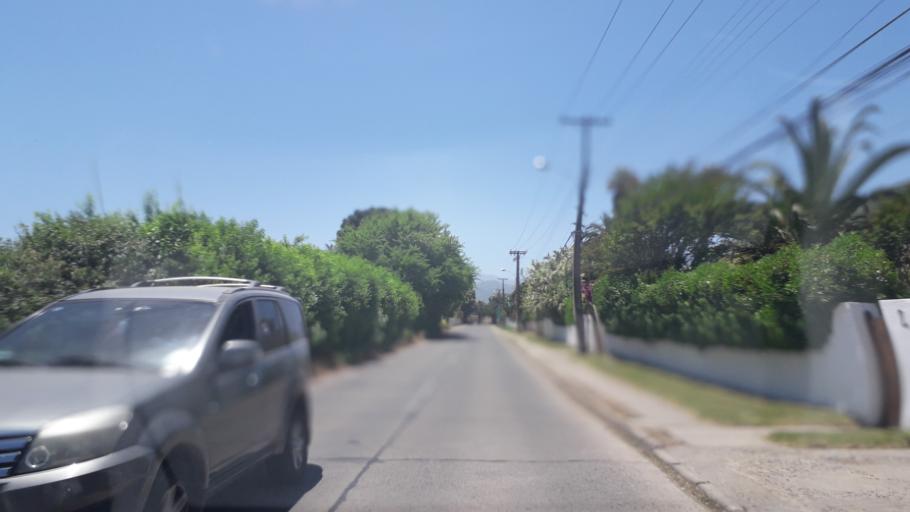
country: CL
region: Valparaiso
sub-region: Provincia de Quillota
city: Quillota
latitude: -32.9163
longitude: -71.2344
